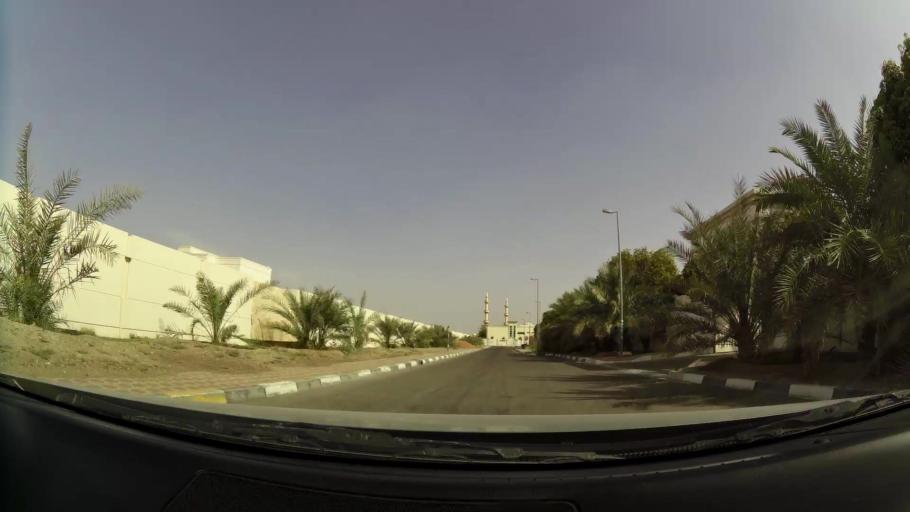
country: AE
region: Abu Dhabi
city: Al Ain
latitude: 24.2450
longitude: 55.6866
